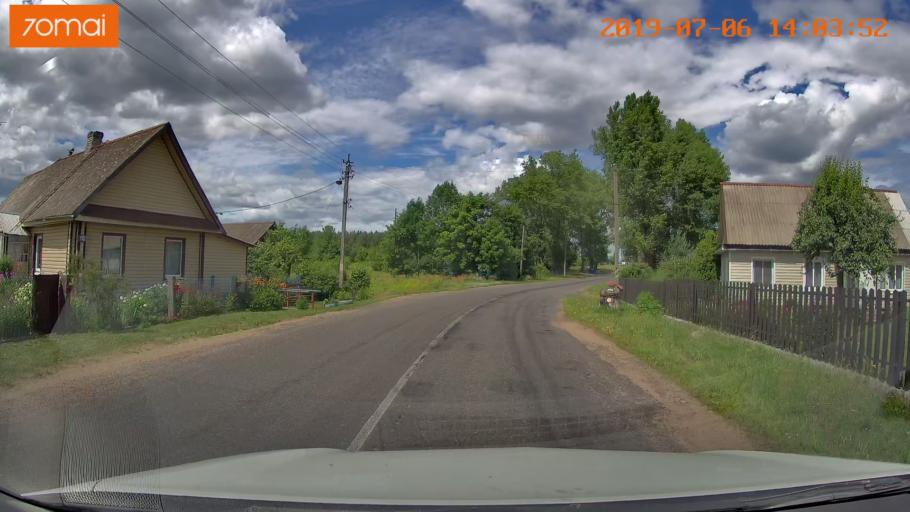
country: BY
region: Minsk
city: Ivyanyets
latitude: 53.8341
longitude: 26.8003
